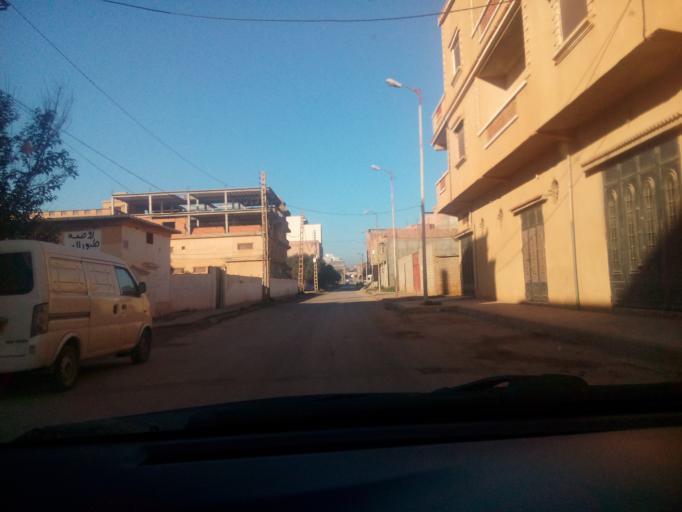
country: DZ
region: Oran
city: Bir el Djir
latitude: 35.7560
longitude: -0.5337
